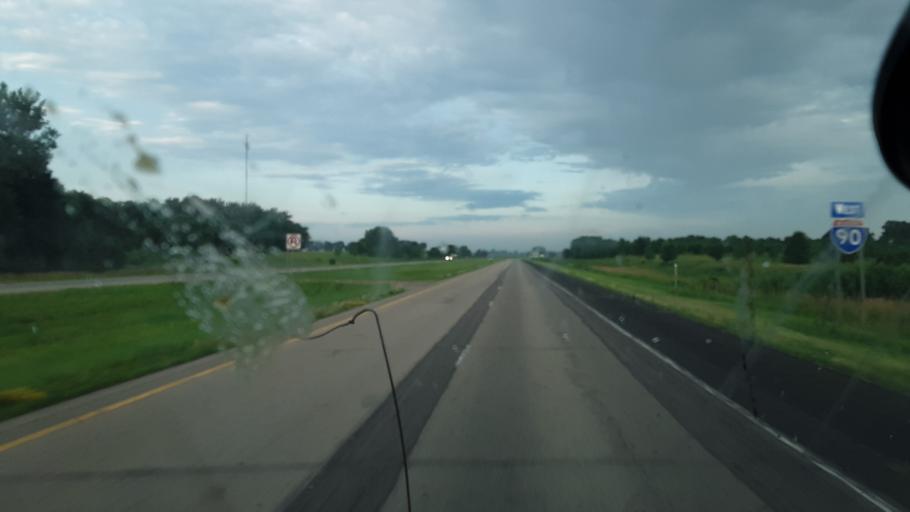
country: US
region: Minnesota
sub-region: Faribault County
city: Wells
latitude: 43.6557
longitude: -93.7373
